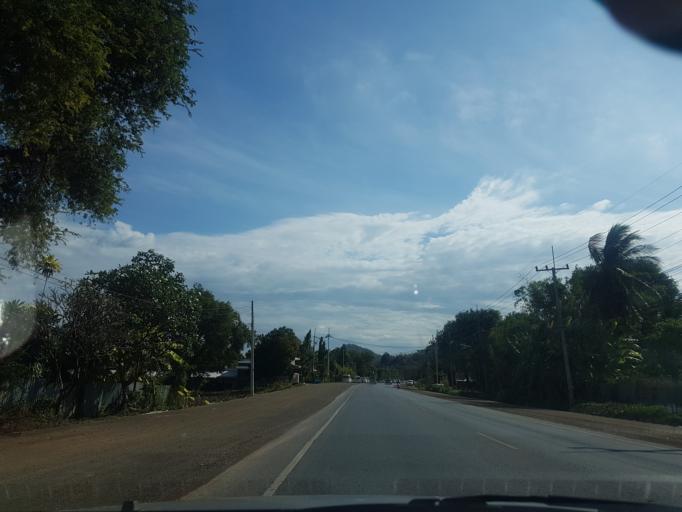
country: TH
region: Sara Buri
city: Phra Phutthabat
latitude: 14.8025
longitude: 100.7499
